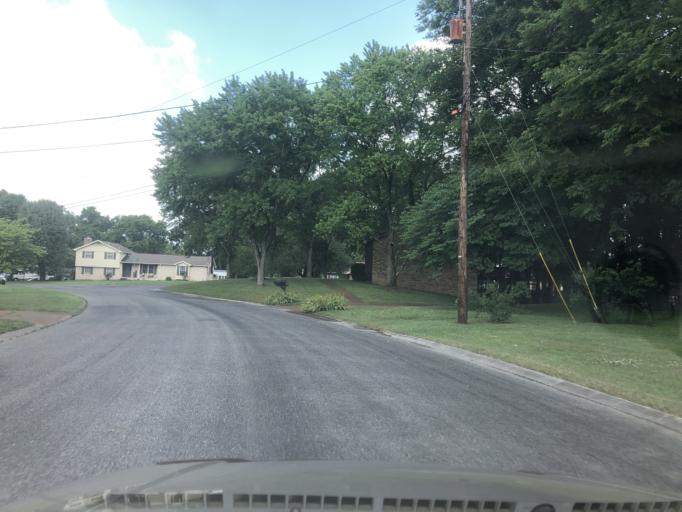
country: US
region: Tennessee
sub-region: Wilson County
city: Green Hill
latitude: 36.2328
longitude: -86.5925
